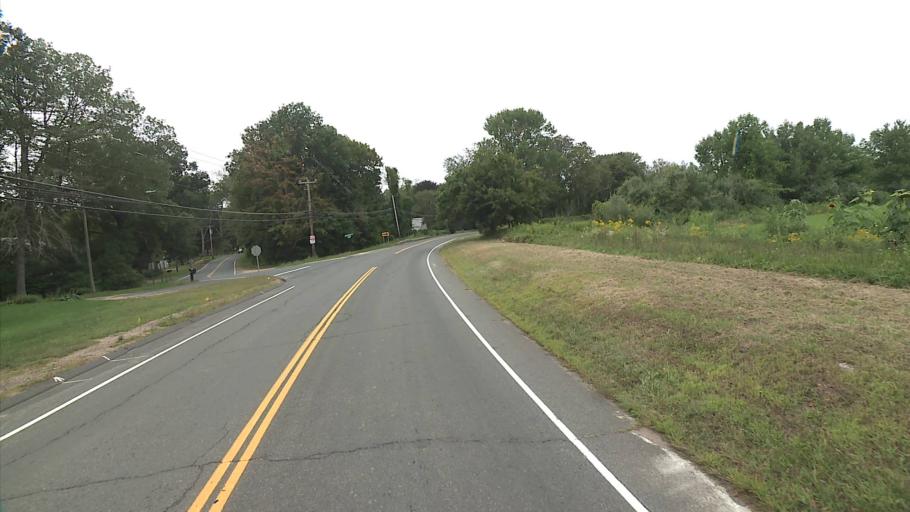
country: US
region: Connecticut
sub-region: Hartford County
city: Manchester
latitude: 41.7706
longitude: -72.4475
